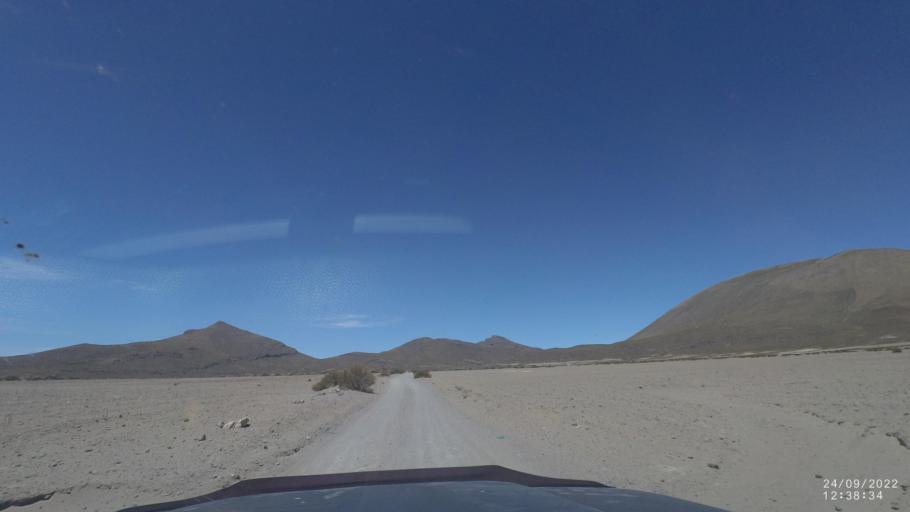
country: BO
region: Potosi
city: Colchani
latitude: -19.7902
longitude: -67.5843
